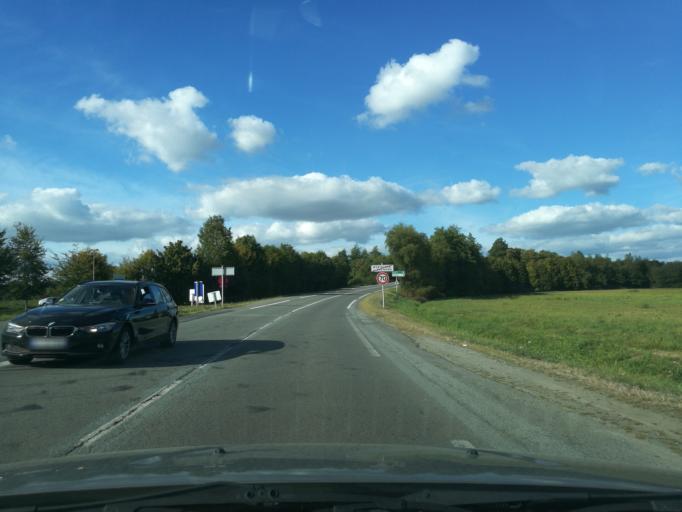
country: FR
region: Brittany
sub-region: Departement d'Ille-et-Vilaine
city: Montauban-de-Bretagne
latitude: 48.2050
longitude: -2.0472
